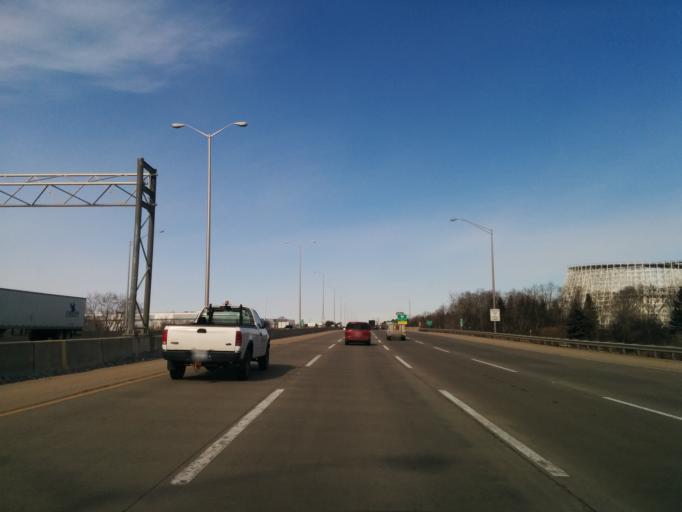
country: US
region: Illinois
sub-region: Lake County
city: Gurnee
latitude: 42.3624
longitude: -87.9382
